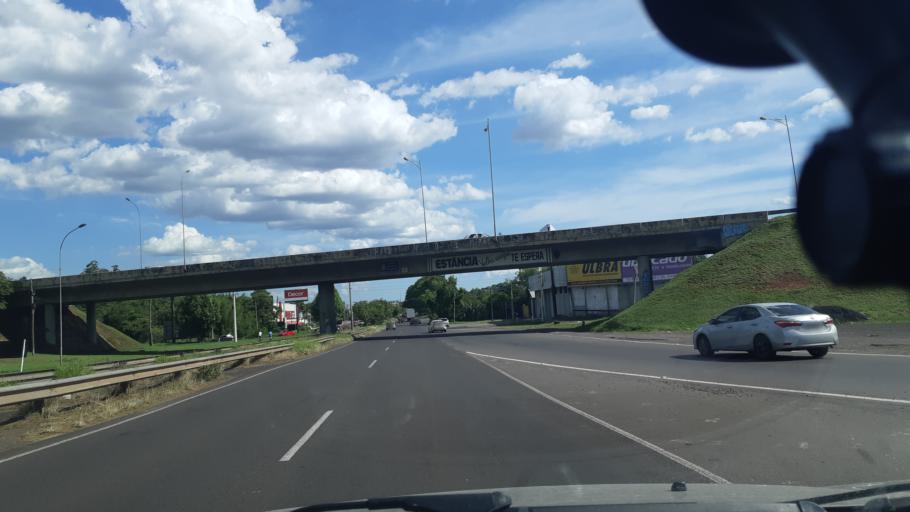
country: BR
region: Rio Grande do Sul
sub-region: Novo Hamburgo
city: Novo Hamburgo
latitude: -29.6568
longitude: -51.1444
